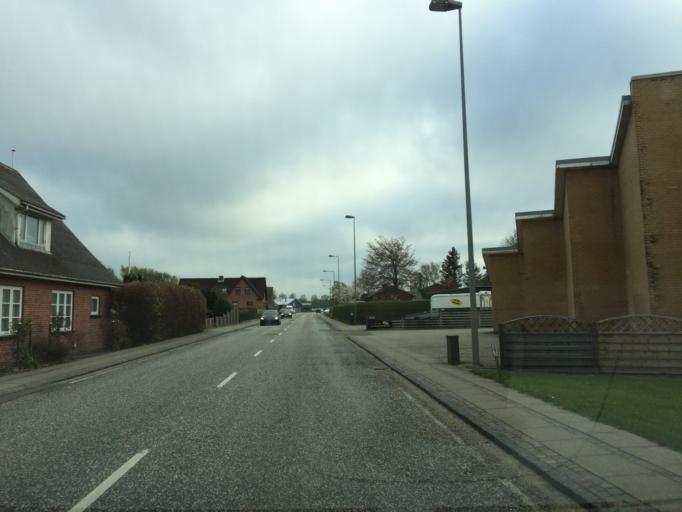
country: DK
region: Central Jutland
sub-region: Herning Kommune
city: Avlum
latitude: 56.2602
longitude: 8.7932
